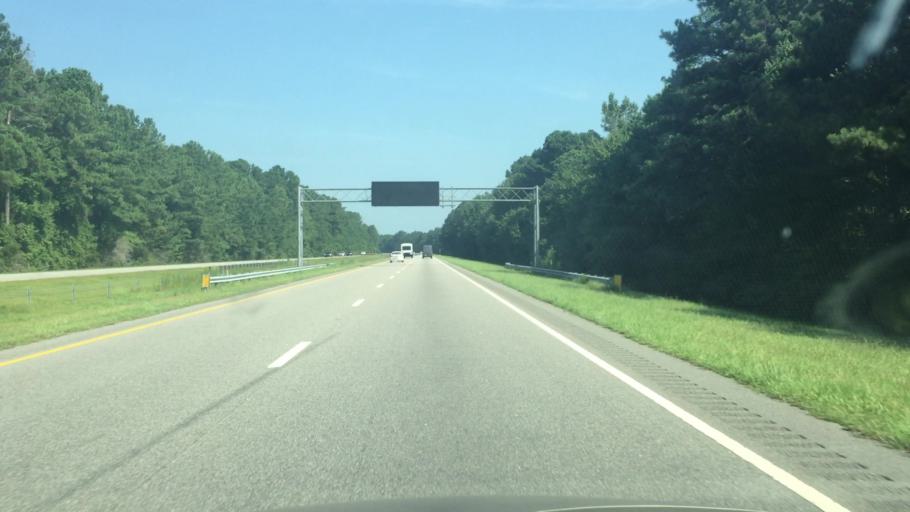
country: US
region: North Carolina
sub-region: Robeson County
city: Lumberton
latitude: 34.5576
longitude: -79.0257
